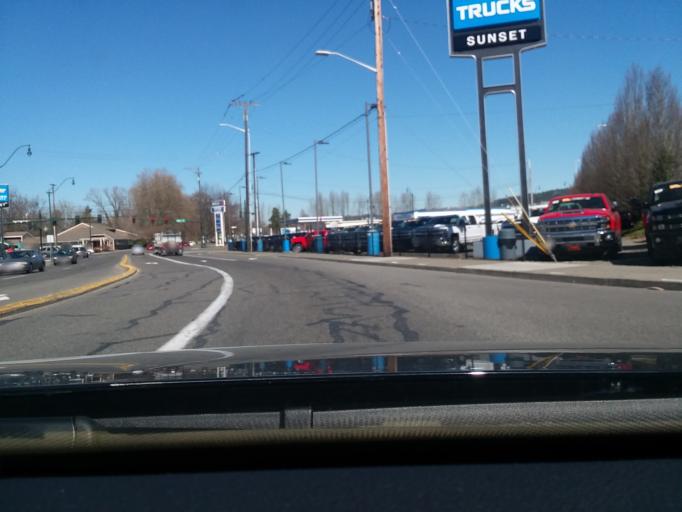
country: US
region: Washington
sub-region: Pierce County
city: Sumner
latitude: 47.2023
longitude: -122.2443
